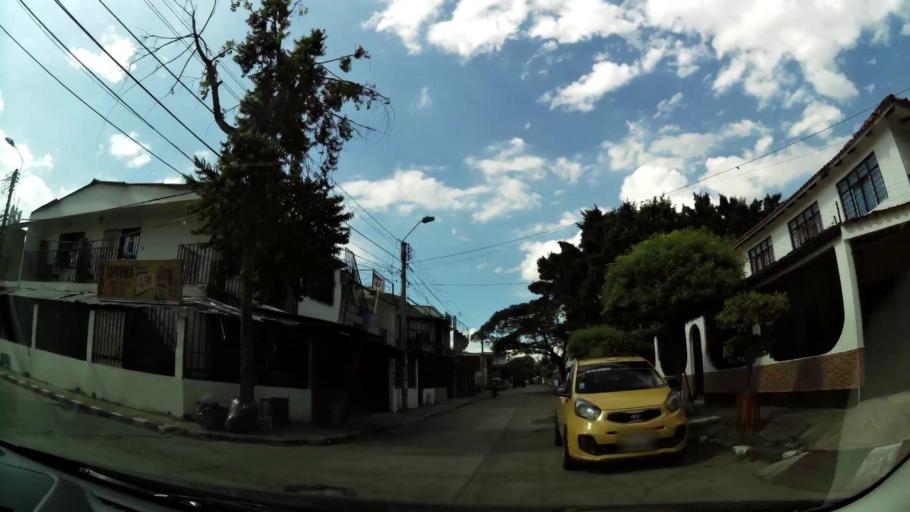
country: CO
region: Valle del Cauca
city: Cali
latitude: 3.4157
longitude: -76.5158
